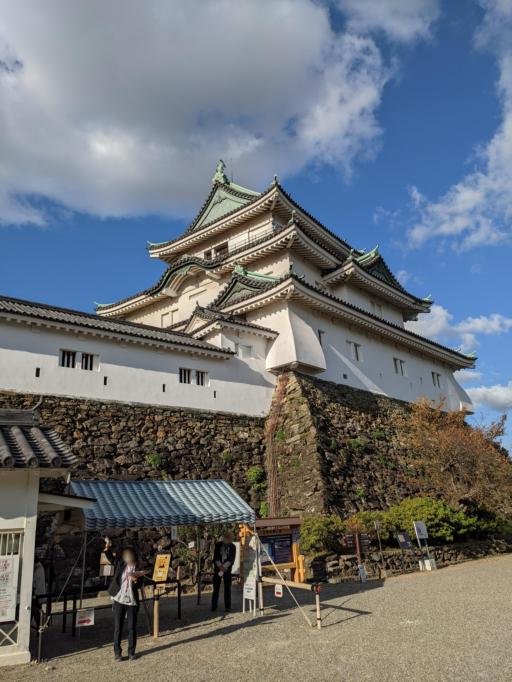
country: JP
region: Wakayama
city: Wakayama-shi
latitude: 34.2272
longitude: 135.1713
